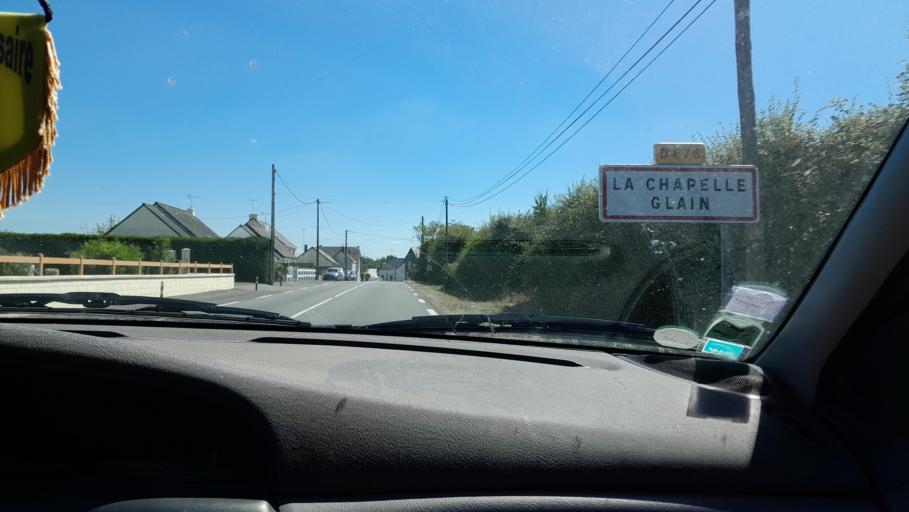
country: FR
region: Pays de la Loire
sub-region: Departement de la Loire-Atlantique
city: Saint-Mars-la-Jaille
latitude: 47.6281
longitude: -1.2002
